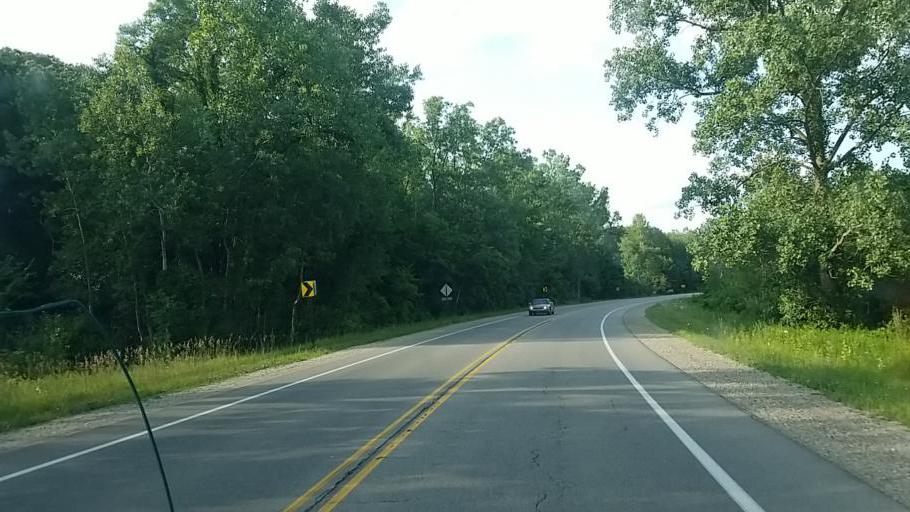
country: US
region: Michigan
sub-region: Kent County
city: Lowell
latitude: 42.9011
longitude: -85.3709
